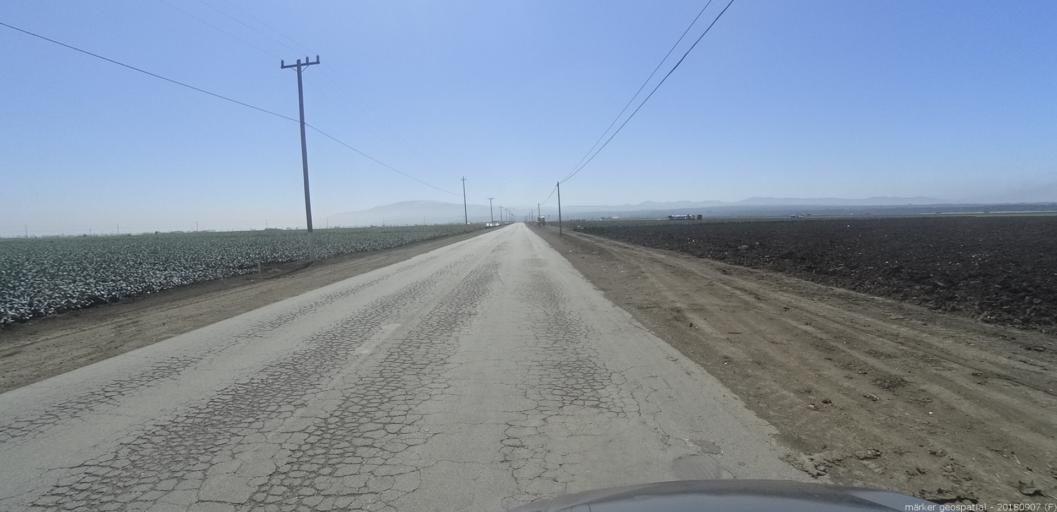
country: US
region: California
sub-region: Monterey County
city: Castroville
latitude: 36.7083
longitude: -121.7379
